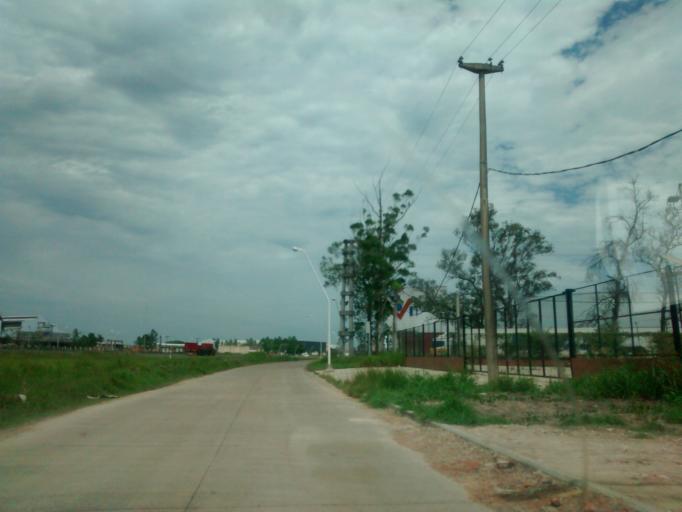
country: AR
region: Chaco
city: Fontana
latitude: -27.4088
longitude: -58.9836
